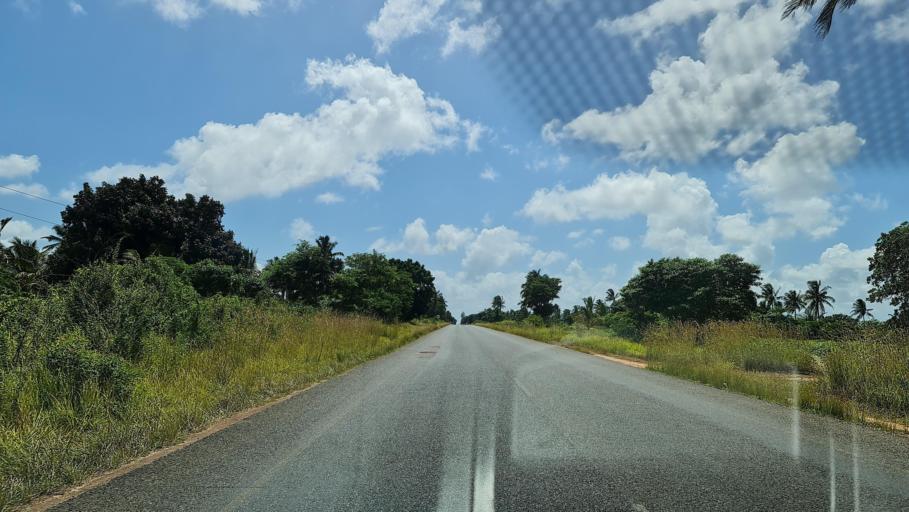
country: MZ
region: Inhambane
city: Maxixe
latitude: -24.5324
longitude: 34.9467
